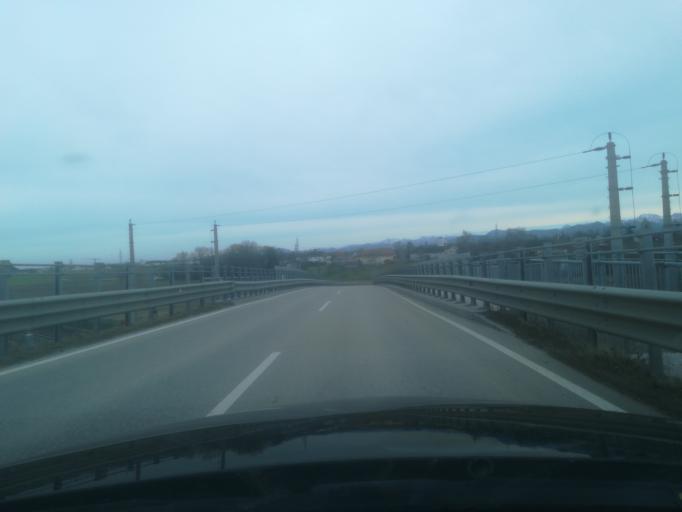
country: AT
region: Upper Austria
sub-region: Wels-Land
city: Neukirchen bei Lambach
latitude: 48.0958
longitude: 13.8354
